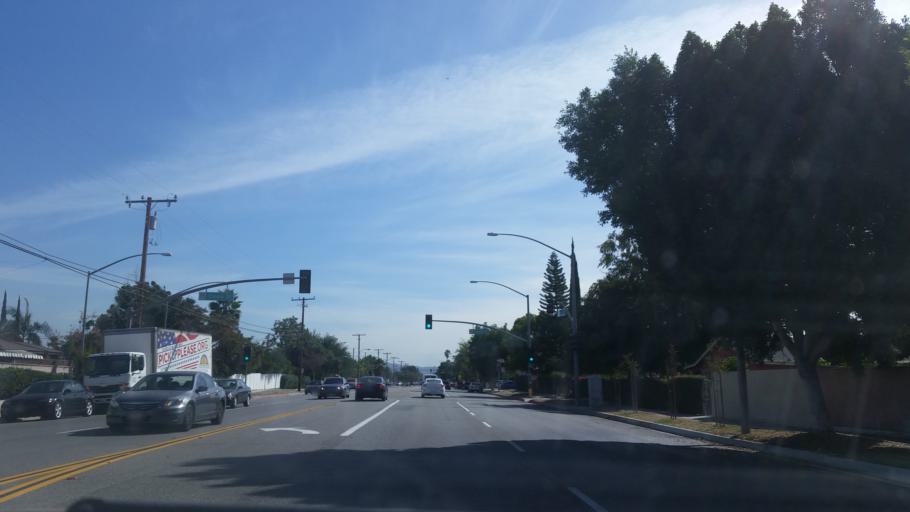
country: US
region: California
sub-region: Los Angeles County
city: Baldwin Park
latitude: 34.1023
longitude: -117.9650
